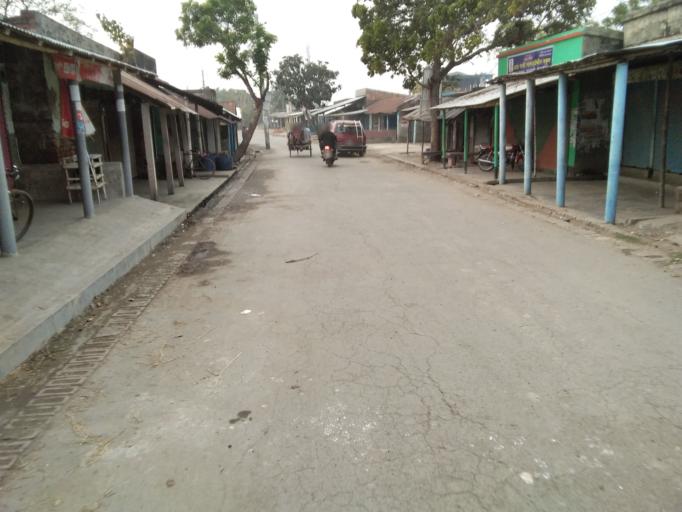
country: BD
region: Khulna
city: Satkhira
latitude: 22.5871
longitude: 89.0645
